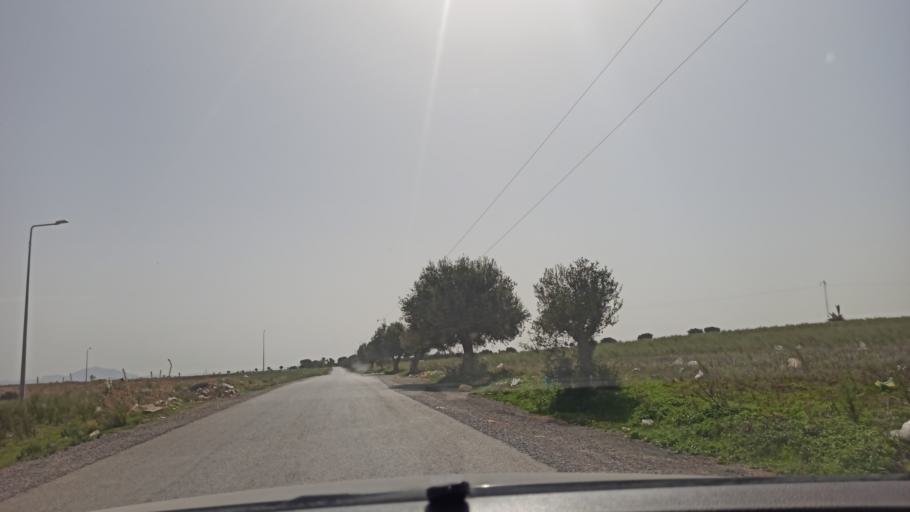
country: TN
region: Manouba
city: Manouba
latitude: 36.7363
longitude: 10.0844
